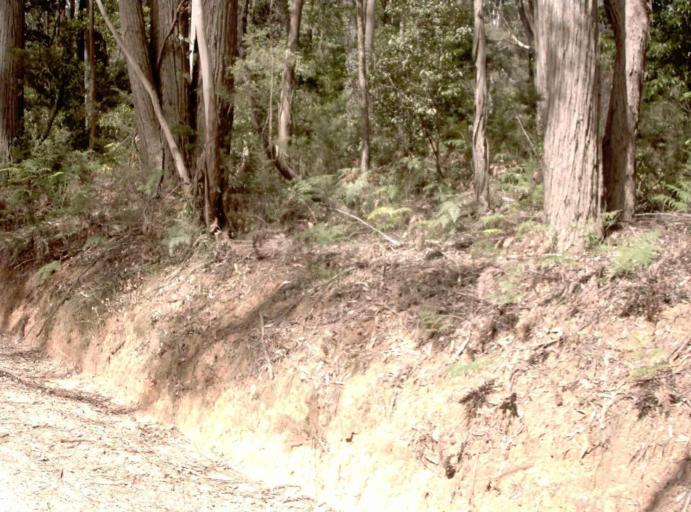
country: AU
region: Victoria
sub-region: East Gippsland
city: Lakes Entrance
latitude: -37.5866
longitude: 148.7259
